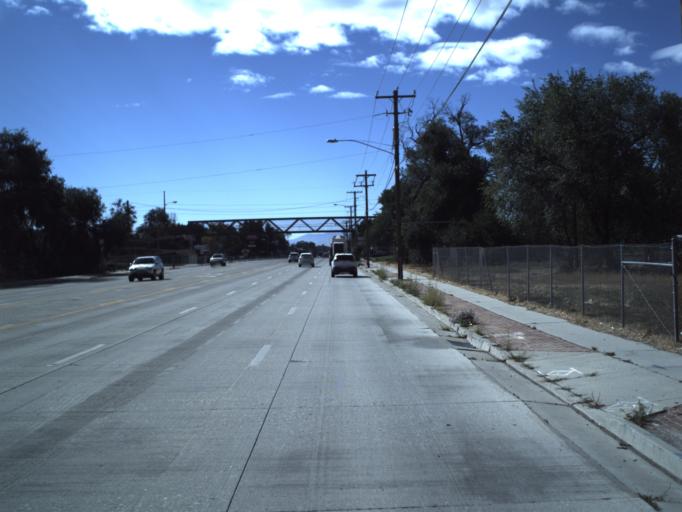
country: US
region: Utah
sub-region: Salt Lake County
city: West Jordan
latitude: 40.6159
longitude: -111.9389
